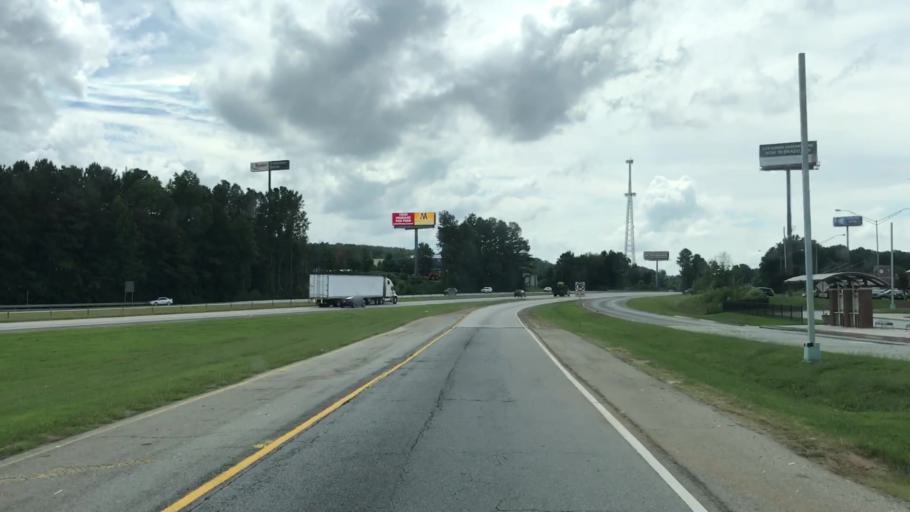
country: US
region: Georgia
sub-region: Gwinnett County
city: Buford
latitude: 34.0856
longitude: -83.9951
